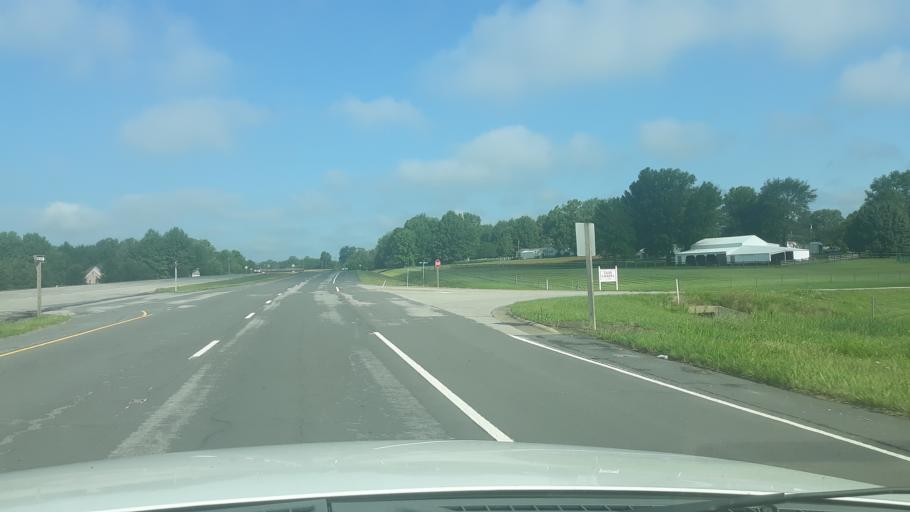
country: US
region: Illinois
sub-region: Saline County
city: Carrier Mills
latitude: 37.7362
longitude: -88.7041
